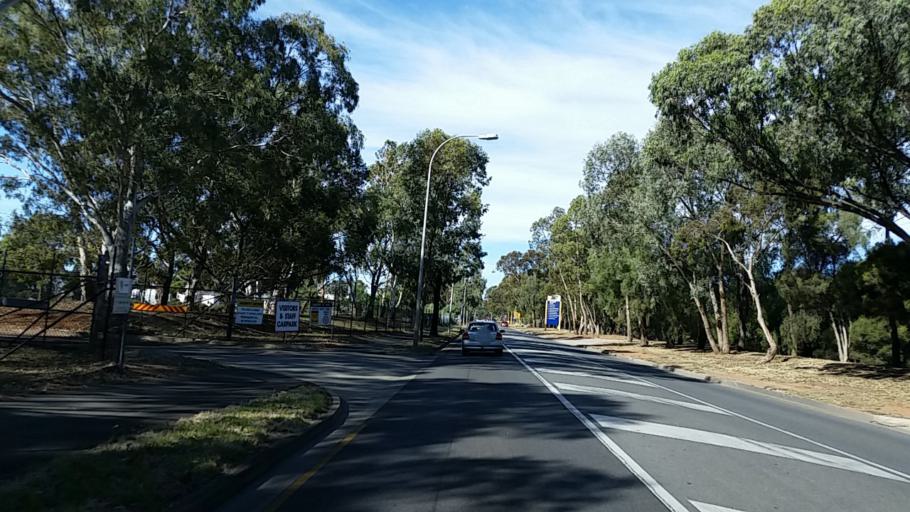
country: AU
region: South Australia
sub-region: Salisbury
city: Salisbury
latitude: -34.7827
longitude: 138.6389
